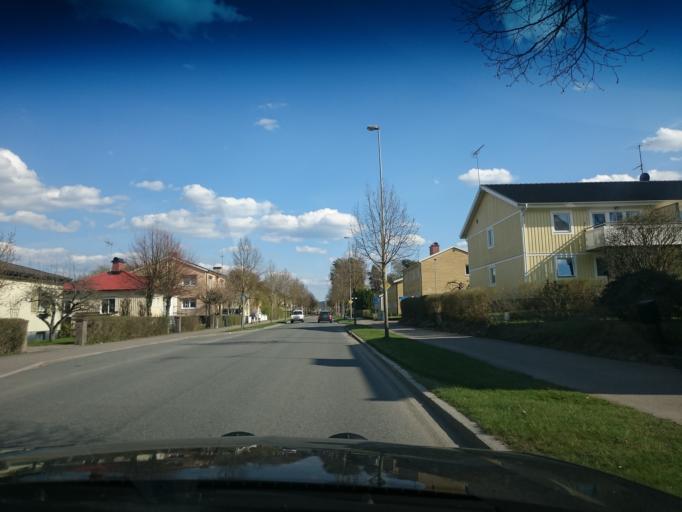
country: SE
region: Joenkoeping
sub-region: Vetlanda Kommun
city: Vetlanda
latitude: 57.4269
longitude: 15.0704
